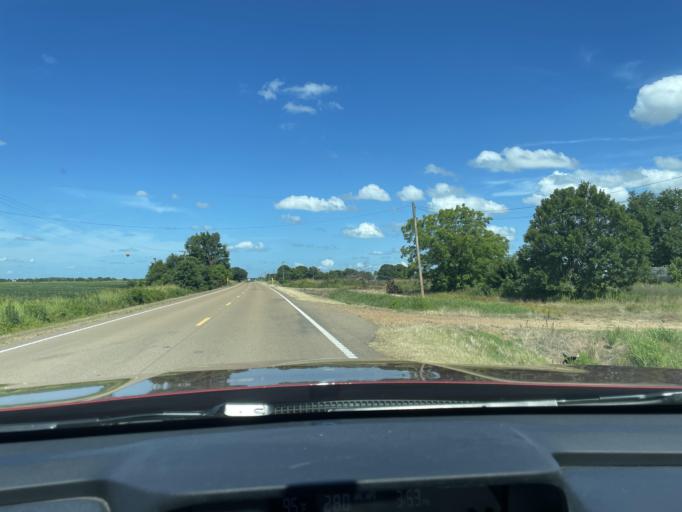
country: US
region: Mississippi
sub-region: Washington County
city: Hollandale
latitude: 33.1843
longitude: -90.6768
